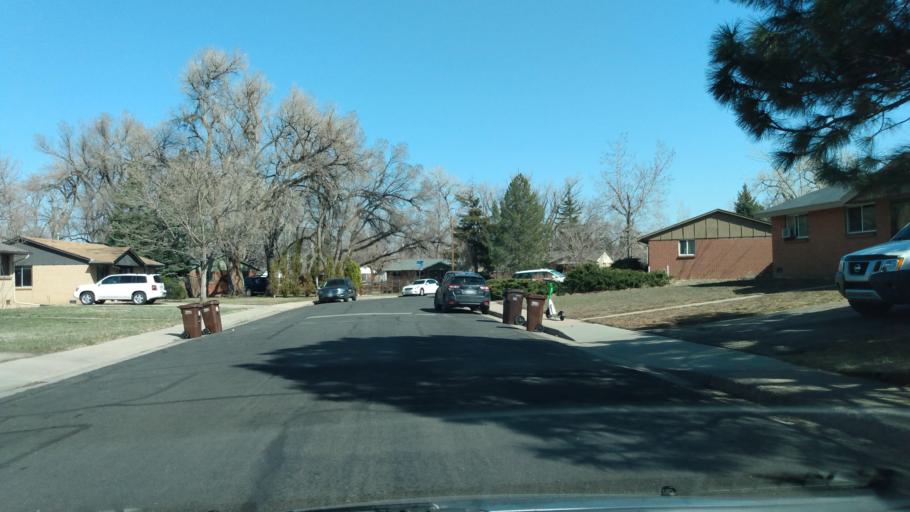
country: US
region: Colorado
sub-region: Boulder County
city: Boulder
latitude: 40.0045
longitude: -105.2518
